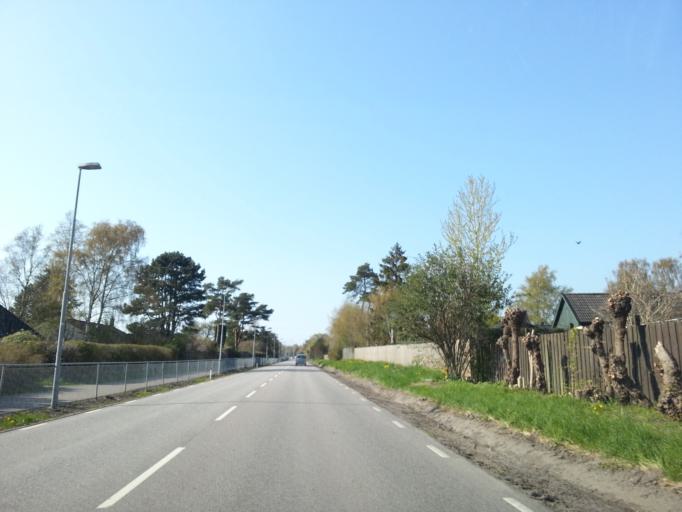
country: SE
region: Skane
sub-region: Vellinge Kommun
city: Hollviken
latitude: 55.4120
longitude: 12.9774
